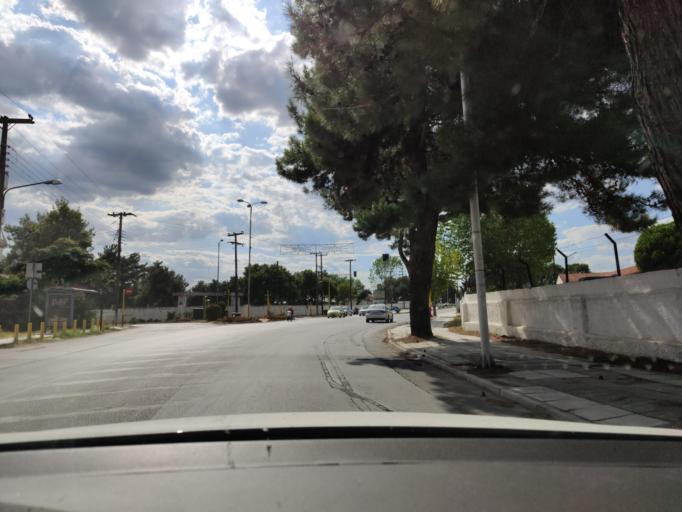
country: GR
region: Central Macedonia
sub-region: Nomos Serron
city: Serres
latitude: 41.0864
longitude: 23.5303
